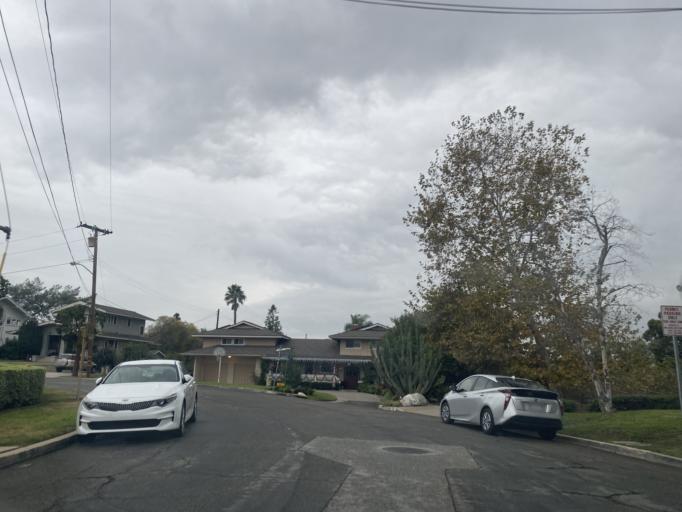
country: US
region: California
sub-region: Orange County
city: Fullerton
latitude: 33.8804
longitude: -117.9209
